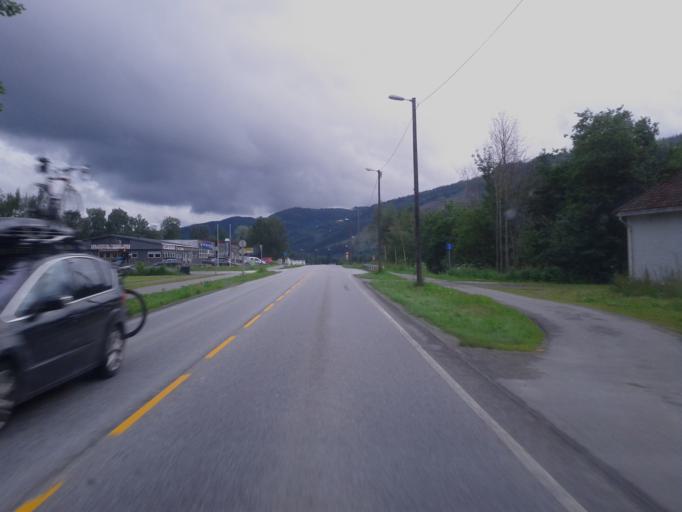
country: NO
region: Sor-Trondelag
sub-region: Melhus
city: Lundamo
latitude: 63.1508
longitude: 10.2776
